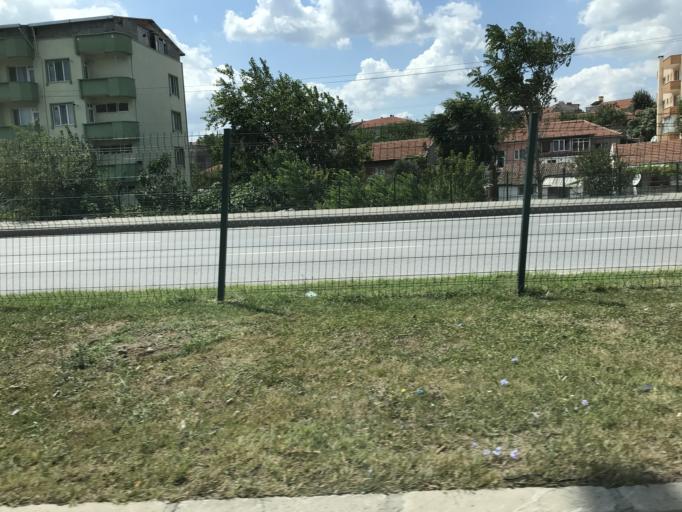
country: TR
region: Balikesir
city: Susurluk
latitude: 39.9105
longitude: 28.1655
